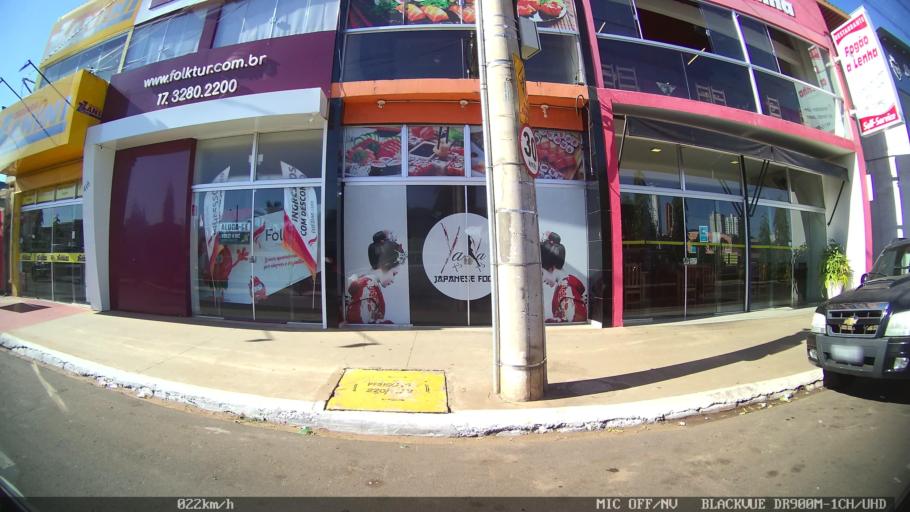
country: BR
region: Sao Paulo
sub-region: Olimpia
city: Olimpia
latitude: -20.7308
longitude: -48.9130
